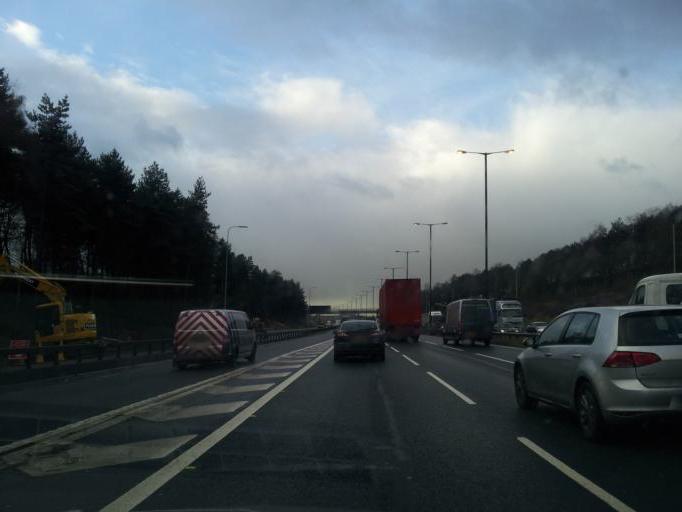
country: GB
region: England
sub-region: Manchester
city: Heywood
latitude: 53.5662
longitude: -2.2348
